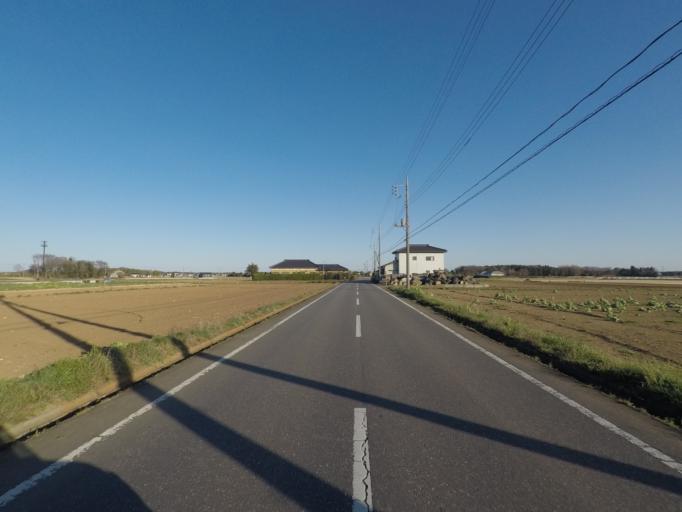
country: JP
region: Ibaraki
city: Ishige
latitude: 36.1325
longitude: 140.0205
